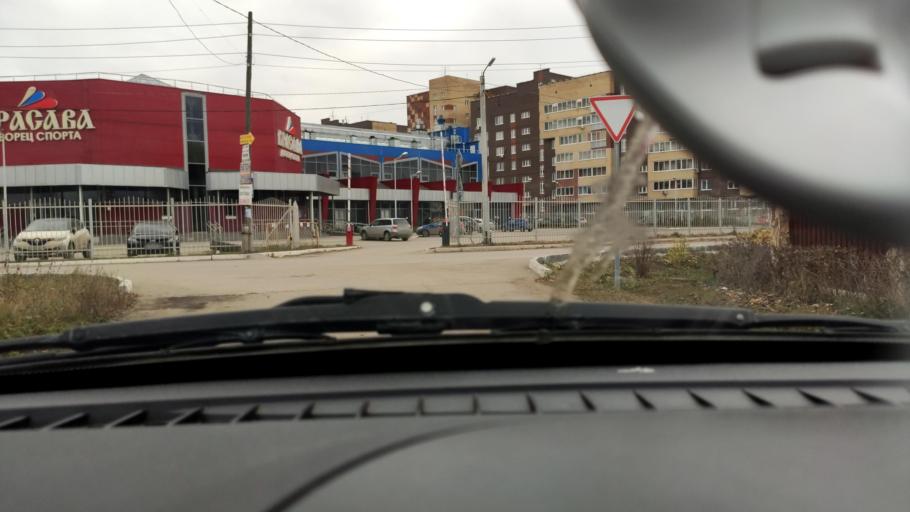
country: RU
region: Perm
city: Kondratovo
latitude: 57.9785
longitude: 56.0989
